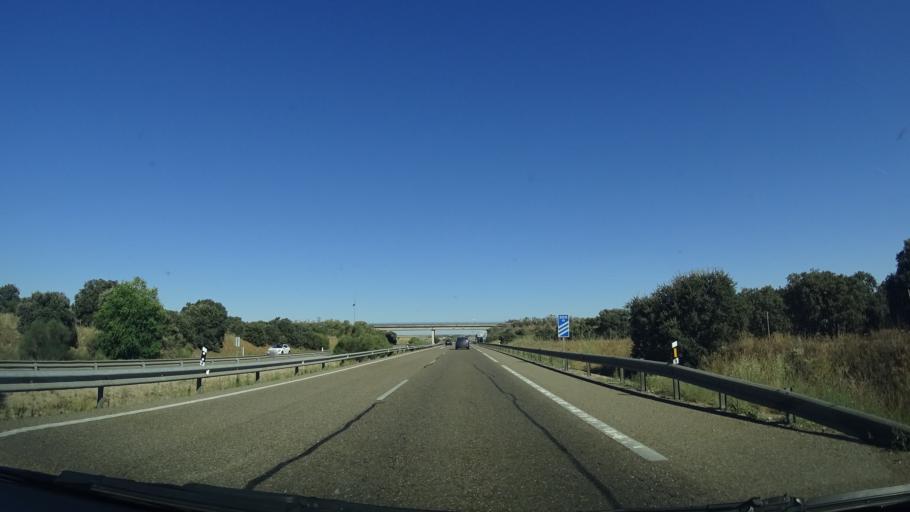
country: ES
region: Castille and Leon
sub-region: Provincia de Valladolid
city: San Pedro de Latarce
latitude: 41.7790
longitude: -5.3167
